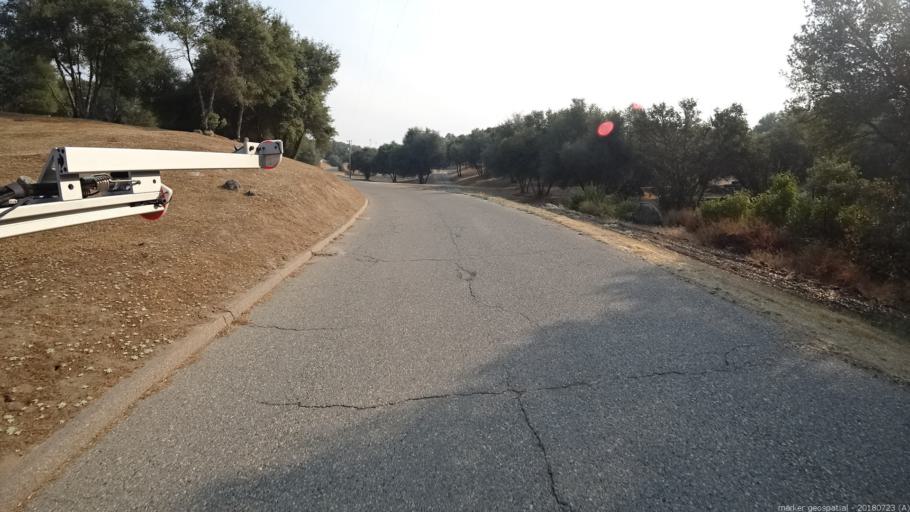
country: US
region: California
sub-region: Madera County
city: Ahwahnee
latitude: 37.3690
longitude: -119.7331
